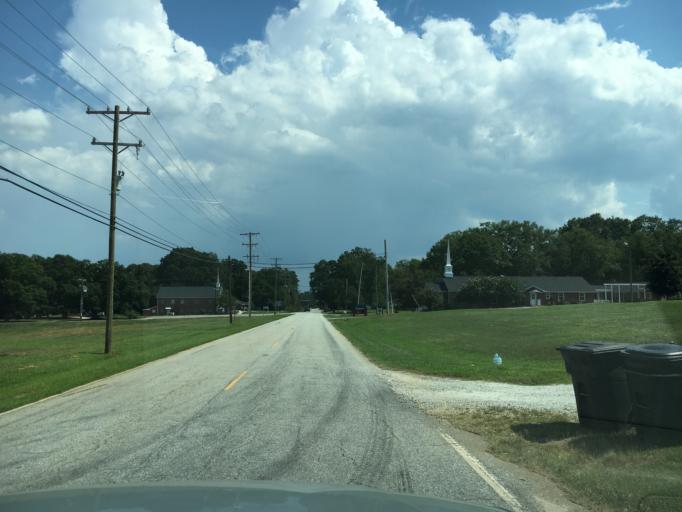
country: US
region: South Carolina
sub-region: Spartanburg County
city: Roebuck
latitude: 34.8357
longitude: -81.9948
